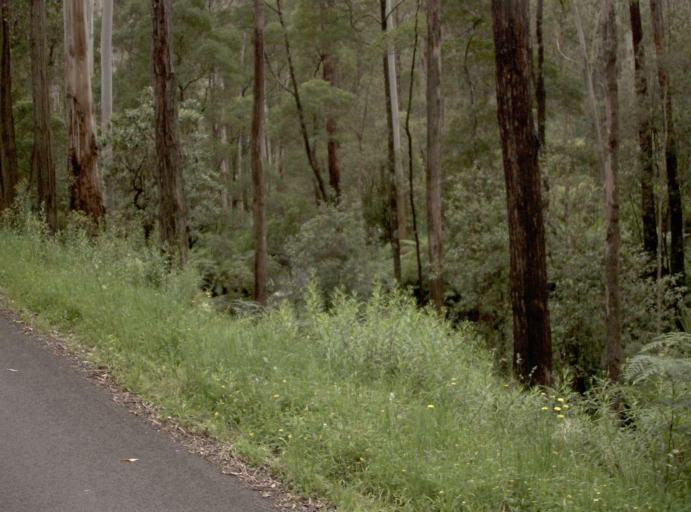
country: AU
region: Victoria
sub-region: Baw Baw
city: Warragul
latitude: -37.9062
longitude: 146.1014
